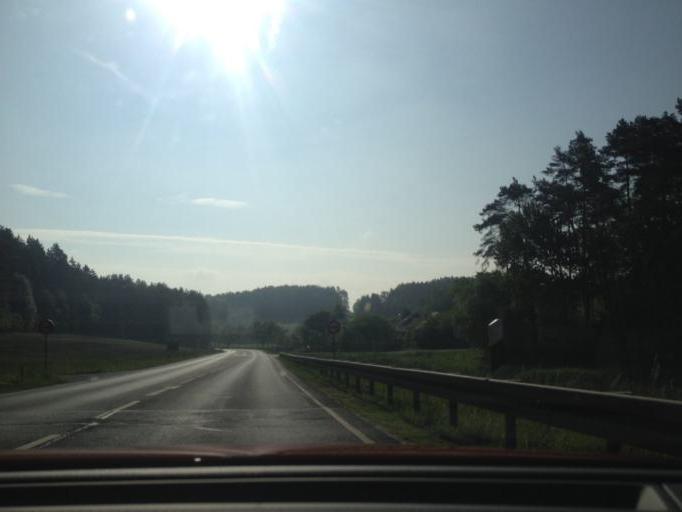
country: DE
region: Bavaria
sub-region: Upper Franconia
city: Pegnitz
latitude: 49.7413
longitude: 11.5198
